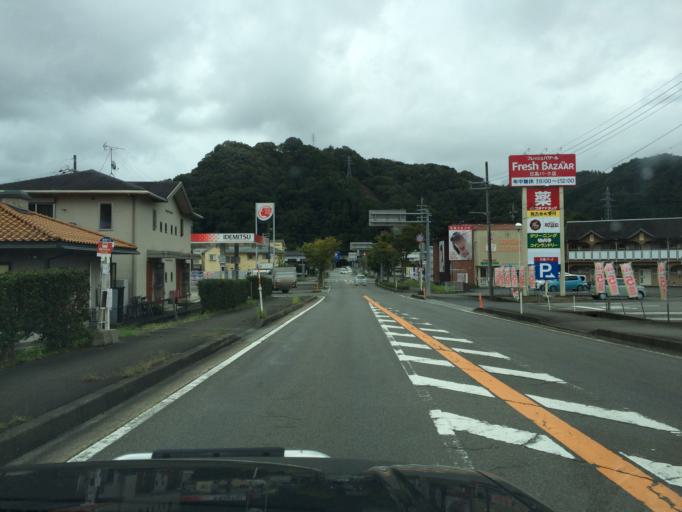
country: JP
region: Hyogo
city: Toyooka
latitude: 35.4687
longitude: 134.7685
